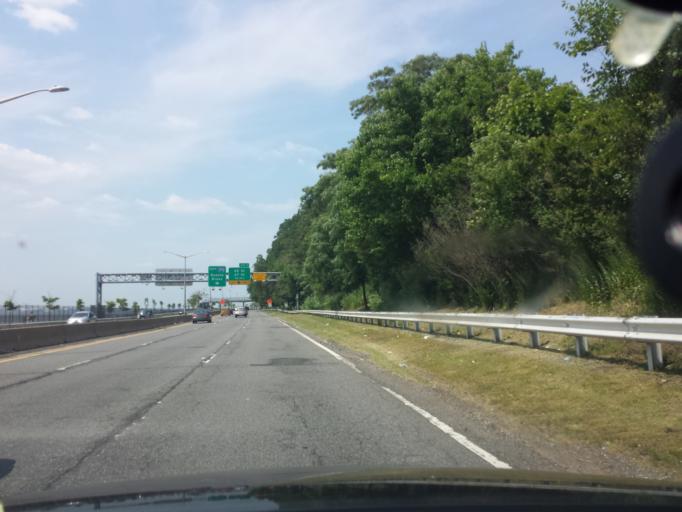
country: US
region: New York
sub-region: Kings County
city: Bensonhurst
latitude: 40.6174
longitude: -74.0404
